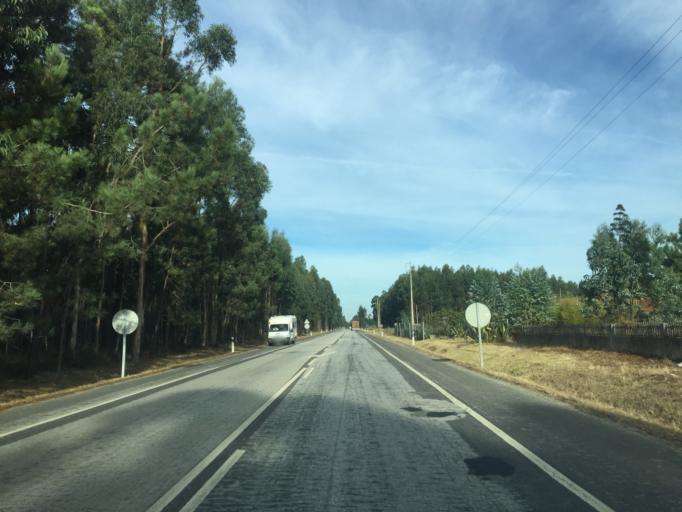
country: PT
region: Coimbra
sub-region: Figueira da Foz
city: Lavos
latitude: 40.0369
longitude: -8.8496
